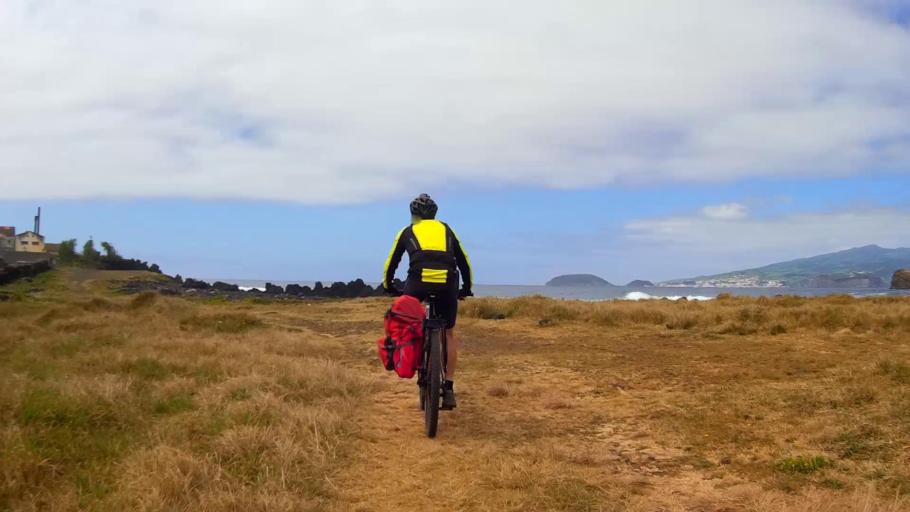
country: PT
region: Azores
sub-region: Madalena
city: Madalena
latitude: 38.5317
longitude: -28.5353
